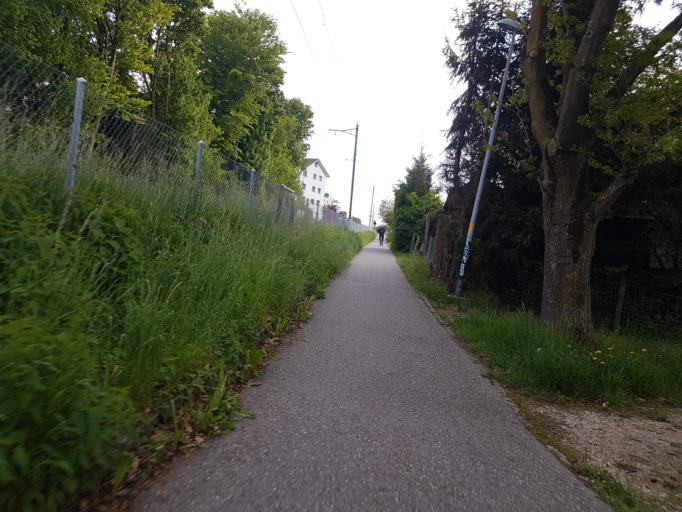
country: CH
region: Bern
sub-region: Biel/Bienne District
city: Nidau
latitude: 47.1182
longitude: 7.2369
